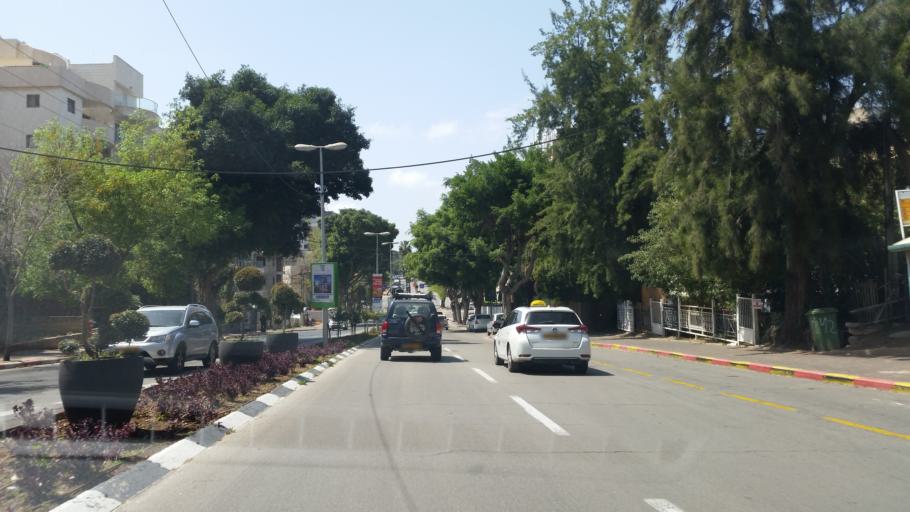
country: IL
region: Central District
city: Ra'anana
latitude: 32.1785
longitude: 34.8840
